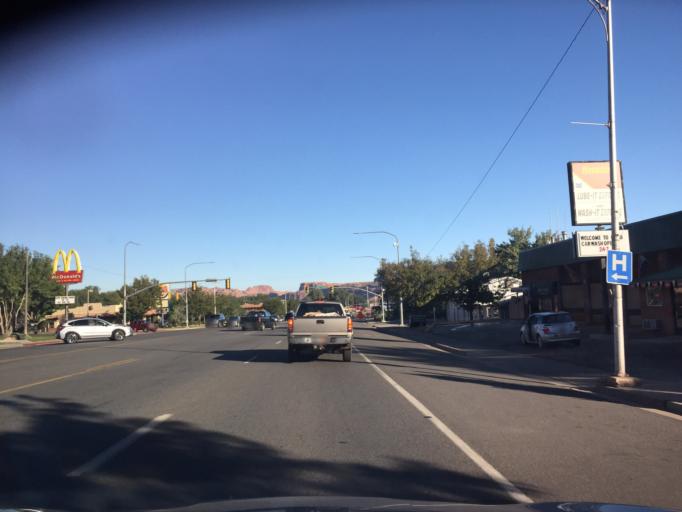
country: US
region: Utah
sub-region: Grand County
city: Moab
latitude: 38.5632
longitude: -109.5491
